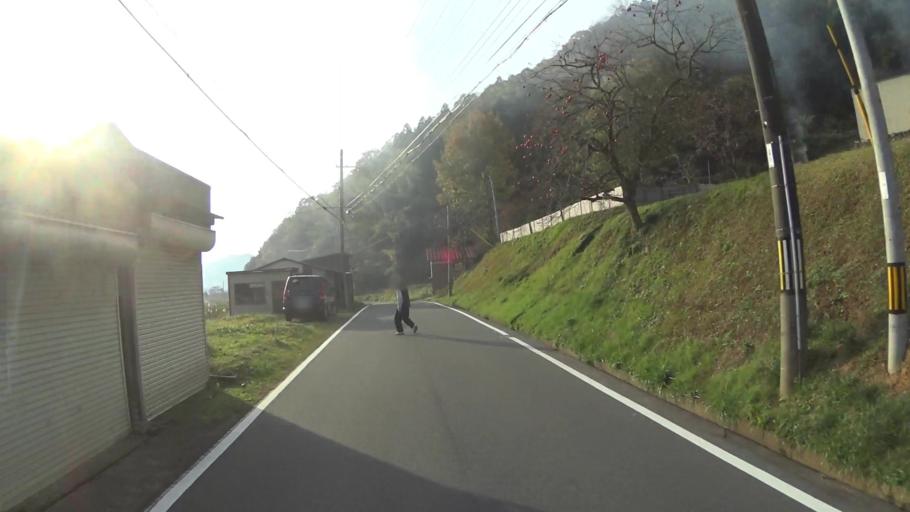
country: JP
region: Kyoto
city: Maizuru
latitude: 35.5281
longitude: 135.4239
